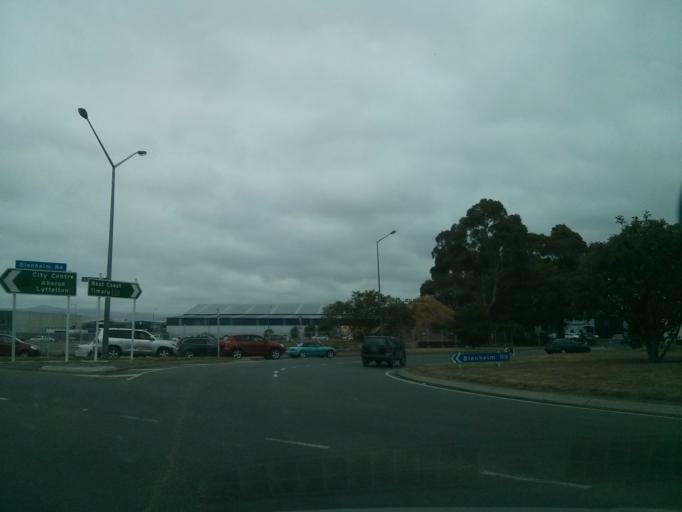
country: NZ
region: Canterbury
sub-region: Selwyn District
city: Prebbleton
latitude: -43.5392
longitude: 172.5544
